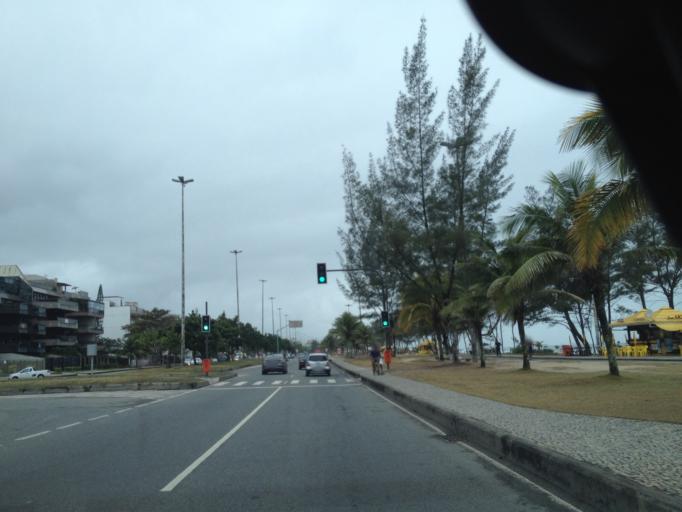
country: BR
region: Rio de Janeiro
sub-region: Nilopolis
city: Nilopolis
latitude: -23.0267
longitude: -43.4619
